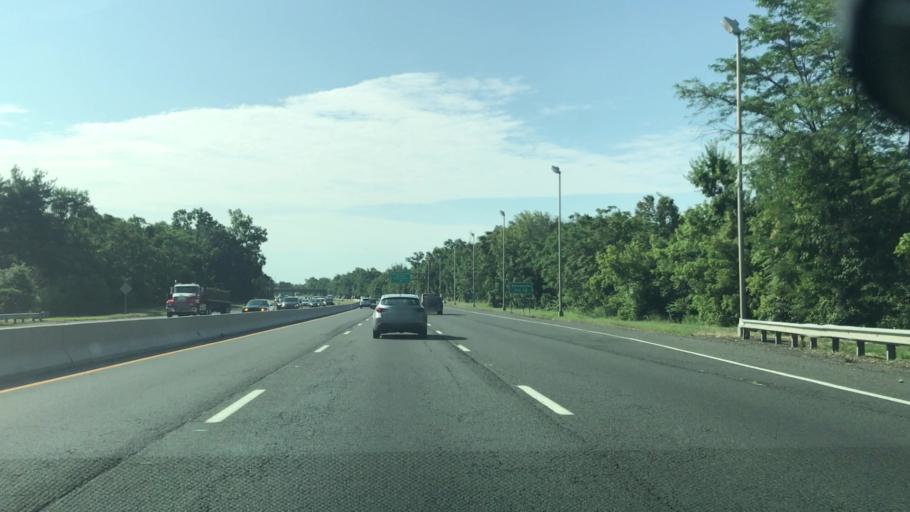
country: US
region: New Jersey
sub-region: Somerset County
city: South Bound Brook
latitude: 40.5532
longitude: -74.5438
